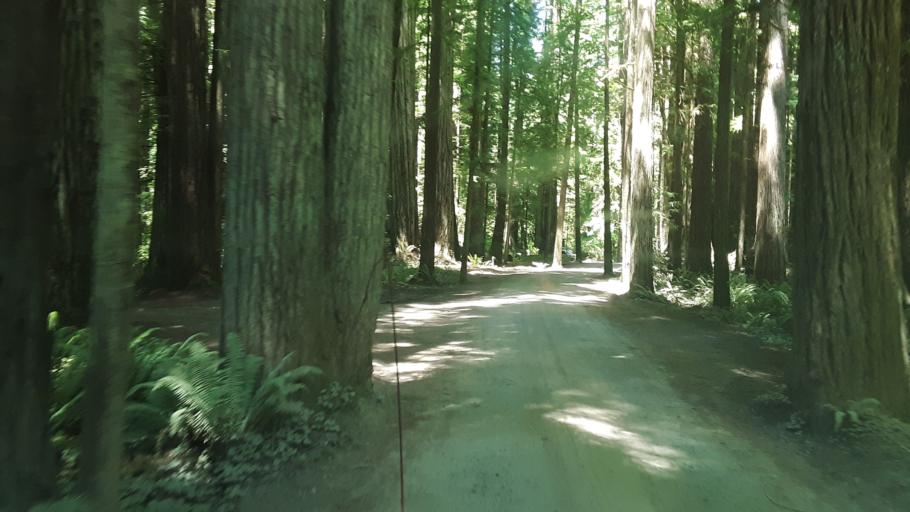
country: US
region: California
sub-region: Del Norte County
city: Bertsch-Oceanview
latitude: 41.8158
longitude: -124.1122
